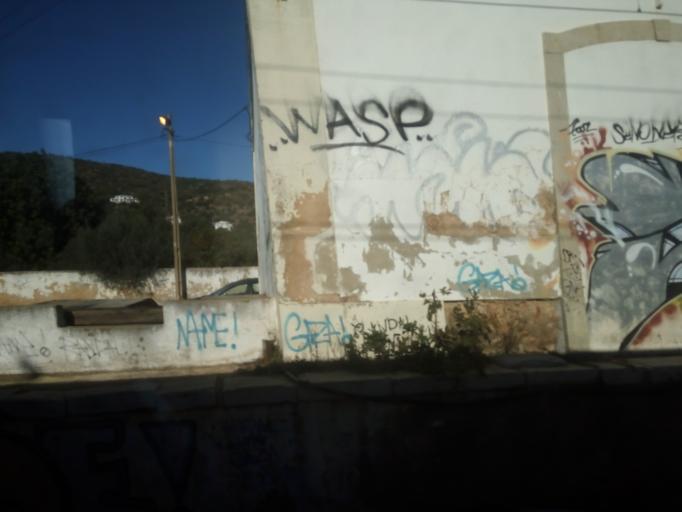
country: PT
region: Faro
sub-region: Loule
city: Almancil
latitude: 37.1045
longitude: -8.0591
